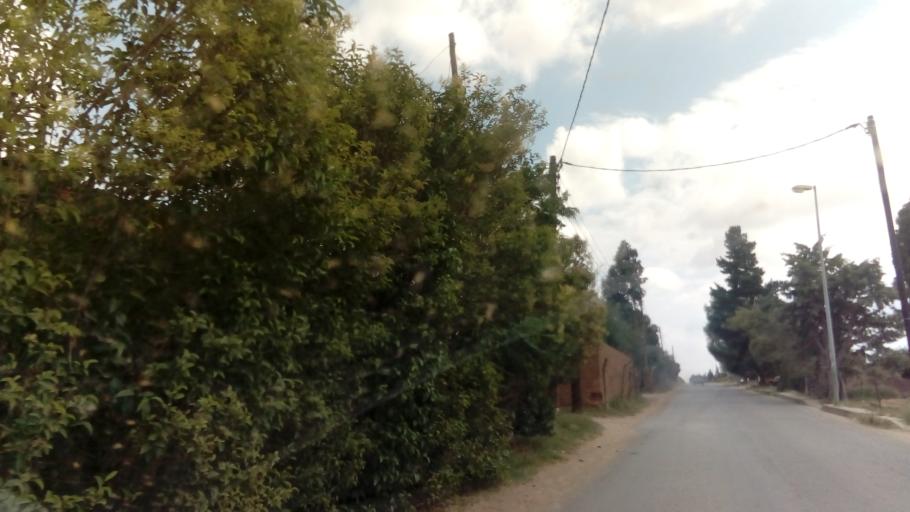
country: LS
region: Maseru
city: Maseru
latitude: -29.3753
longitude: 27.5313
